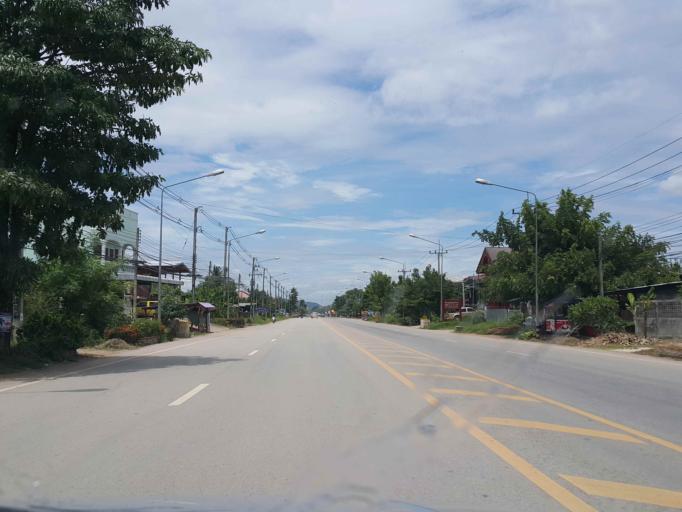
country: TH
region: Sukhothai
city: Ban Na
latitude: 17.0125
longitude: 99.7681
